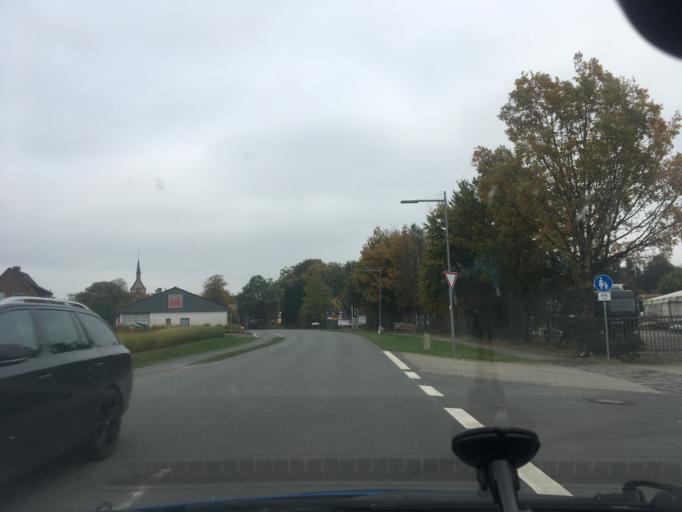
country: DE
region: Lower Saxony
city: Bispingen
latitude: 53.0789
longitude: 9.9962
